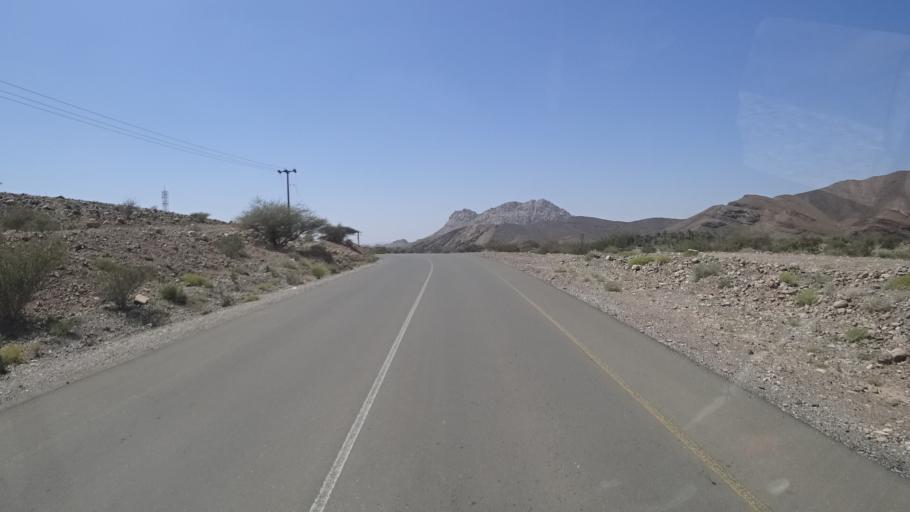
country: OM
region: Az Zahirah
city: `Ibri
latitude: 23.1917
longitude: 56.9262
